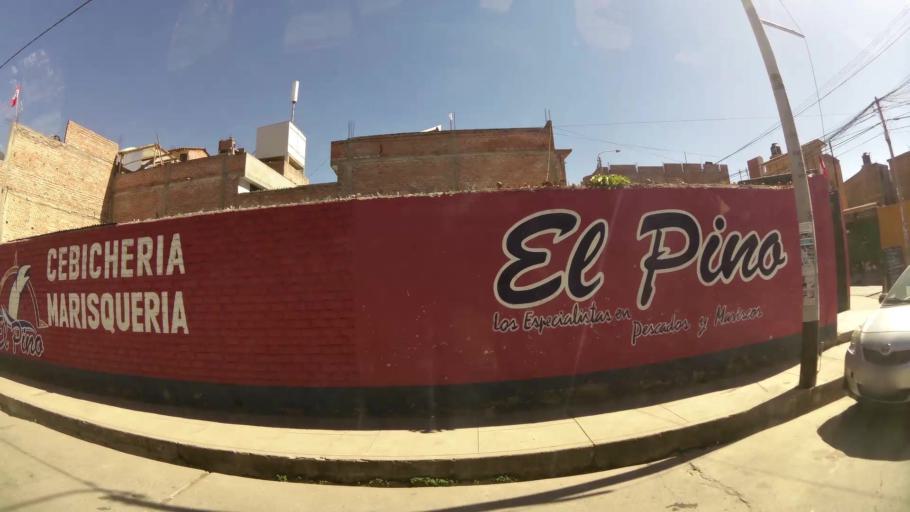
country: PE
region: Ayacucho
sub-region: Provincia de Huamanga
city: Ayacucho
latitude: -13.1491
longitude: -74.2260
